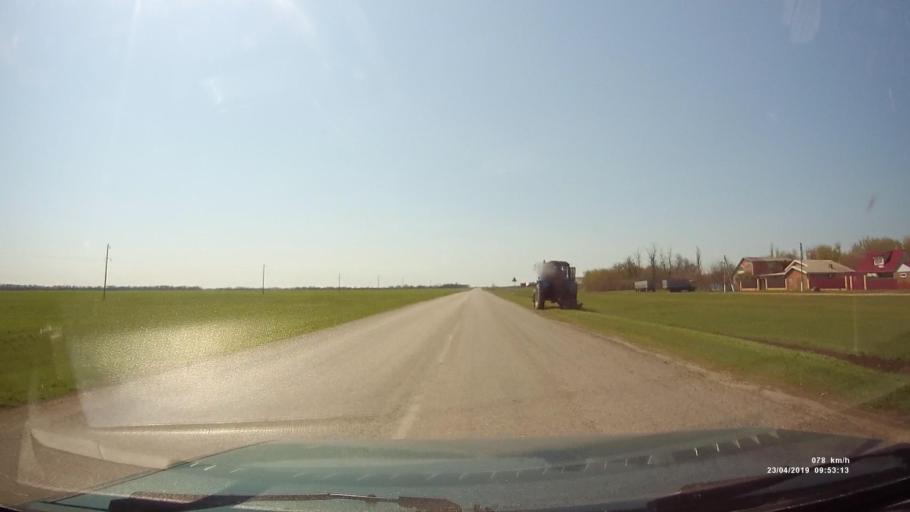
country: RU
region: Rostov
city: Orlovskiy
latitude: 46.8354
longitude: 42.0496
